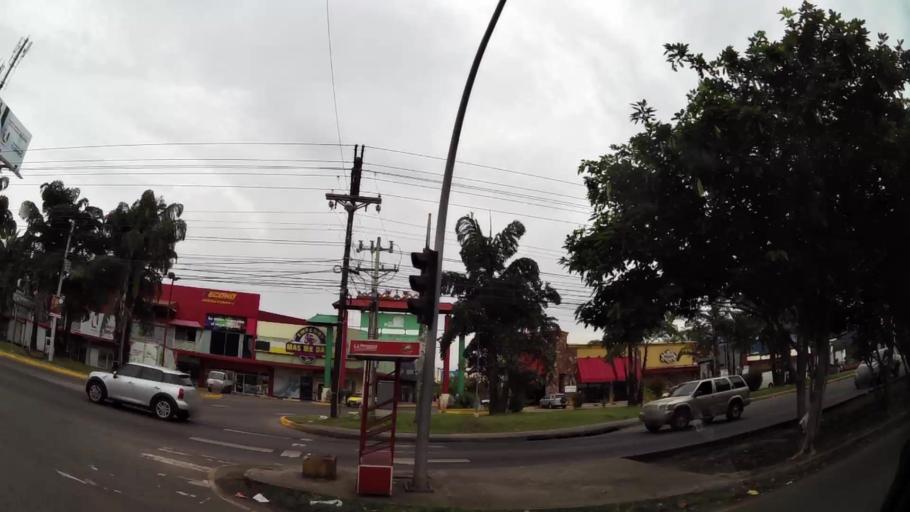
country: PA
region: Panama
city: San Miguelito
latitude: 9.0448
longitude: -79.4530
